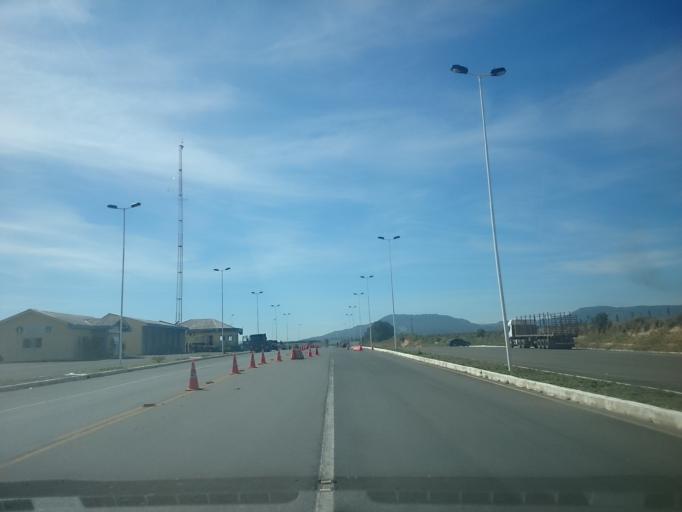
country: BR
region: Santa Catarina
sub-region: Lages
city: Lages
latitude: -27.7698
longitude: -50.1790
